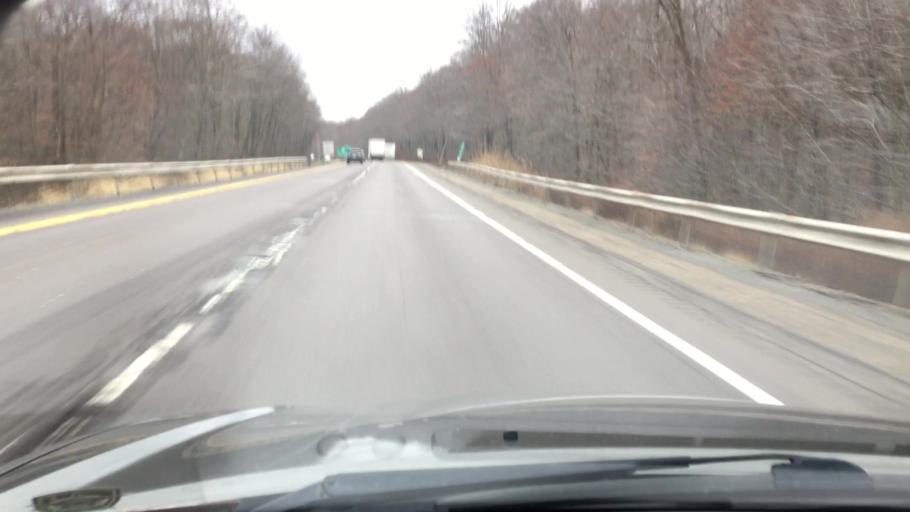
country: US
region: Pennsylvania
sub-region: Luzerne County
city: White Haven
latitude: 41.0598
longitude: -75.7388
